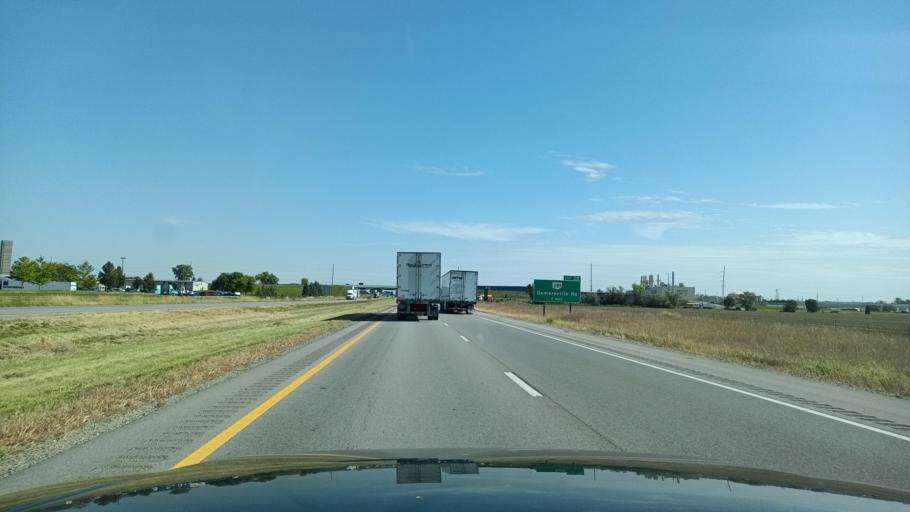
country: US
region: Ohio
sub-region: Defiance County
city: Defiance
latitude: 41.3082
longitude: -84.3471
